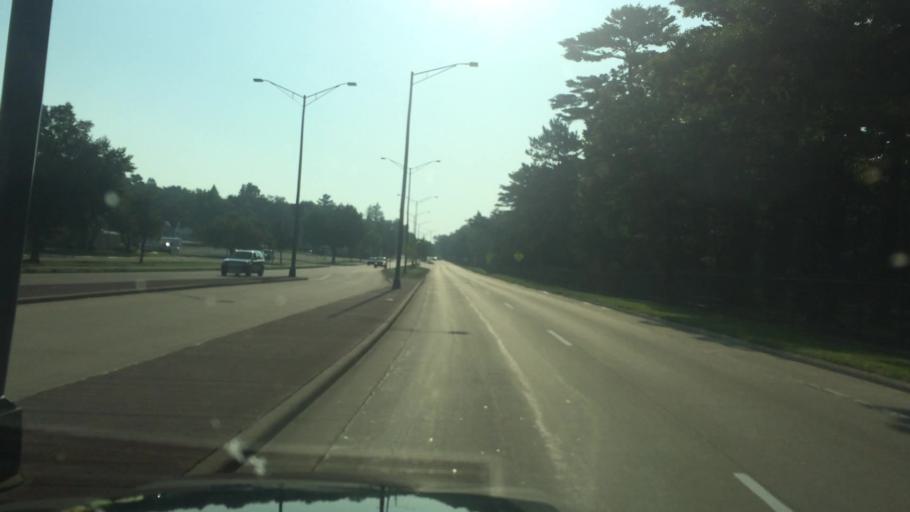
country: US
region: Wisconsin
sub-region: Marathon County
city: Wausau
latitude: 44.9591
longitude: -89.6539
